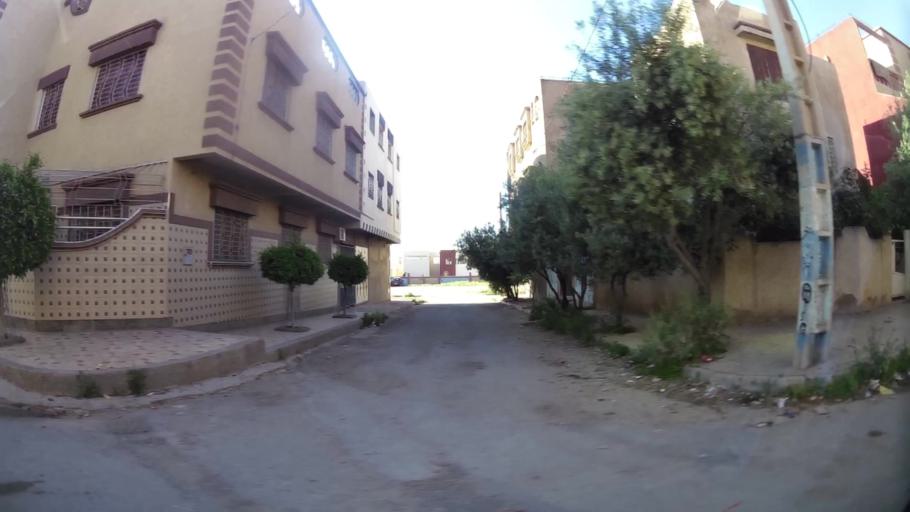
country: MA
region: Oriental
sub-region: Oujda-Angad
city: Oujda
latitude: 34.6694
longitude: -1.9474
